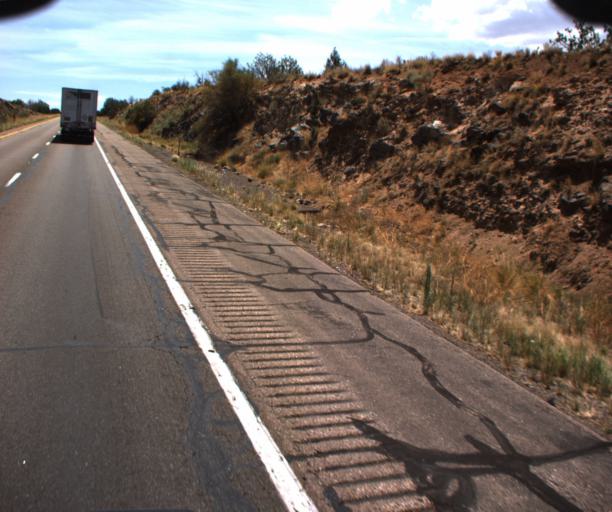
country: US
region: Arizona
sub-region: Yavapai County
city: Paulden
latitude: 35.2800
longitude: -112.7840
